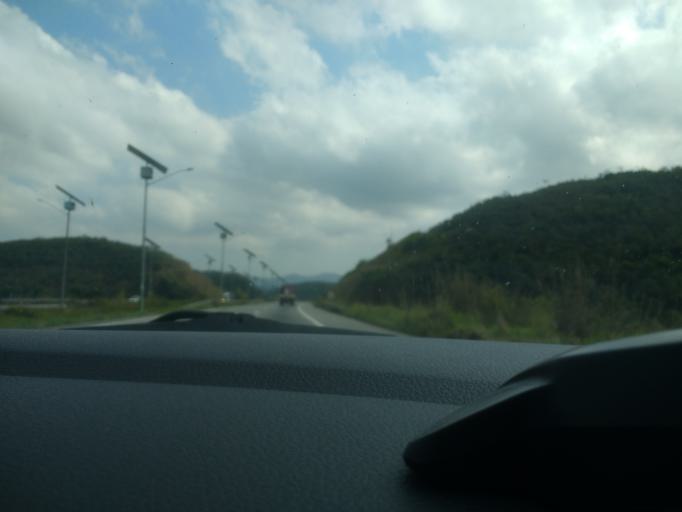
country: BR
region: Rio de Janeiro
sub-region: Queimados
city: Queimados
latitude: -22.6712
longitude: -43.5475
